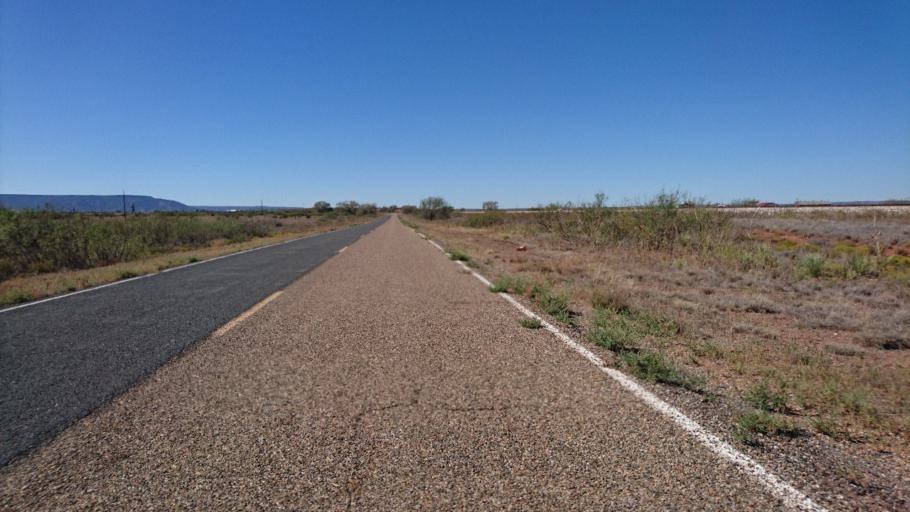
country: US
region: New Mexico
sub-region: Quay County
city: Tucumcari
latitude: 35.0986
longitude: -104.0559
